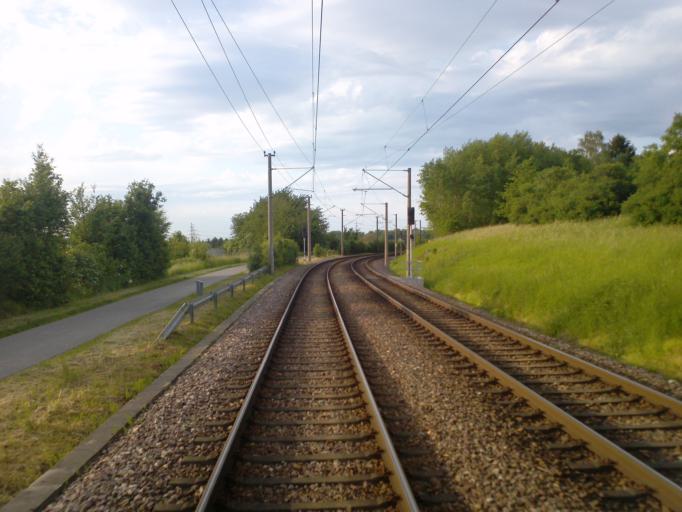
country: DE
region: Baden-Wuerttemberg
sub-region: Karlsruhe Region
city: Ettlingen
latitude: 48.9507
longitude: 8.3987
